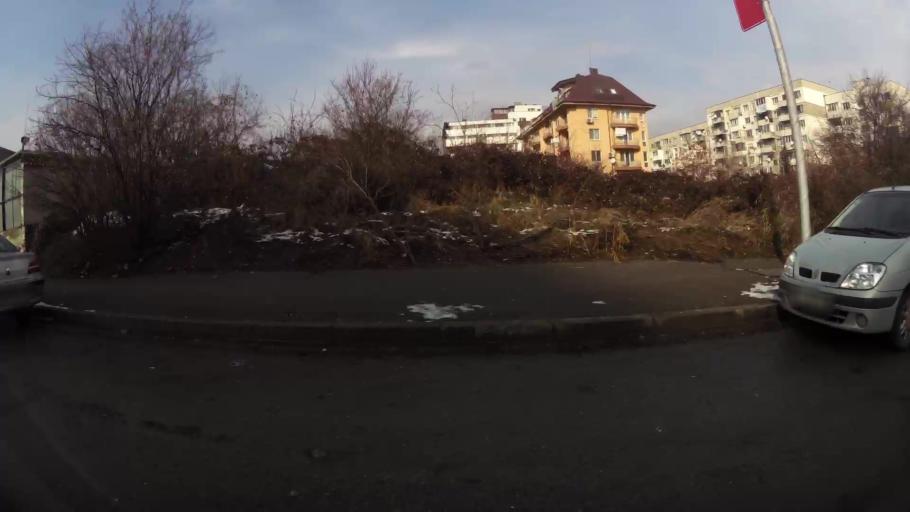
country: BG
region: Sofia-Capital
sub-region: Stolichna Obshtina
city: Sofia
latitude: 42.7175
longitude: 23.2612
